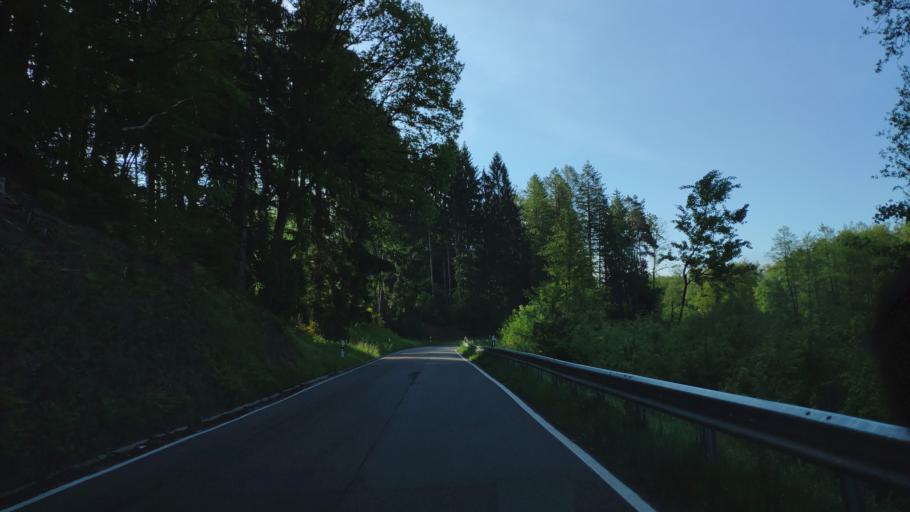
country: DE
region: Rheinland-Pfalz
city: Ludwigswinkel
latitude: 49.0926
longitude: 7.6759
